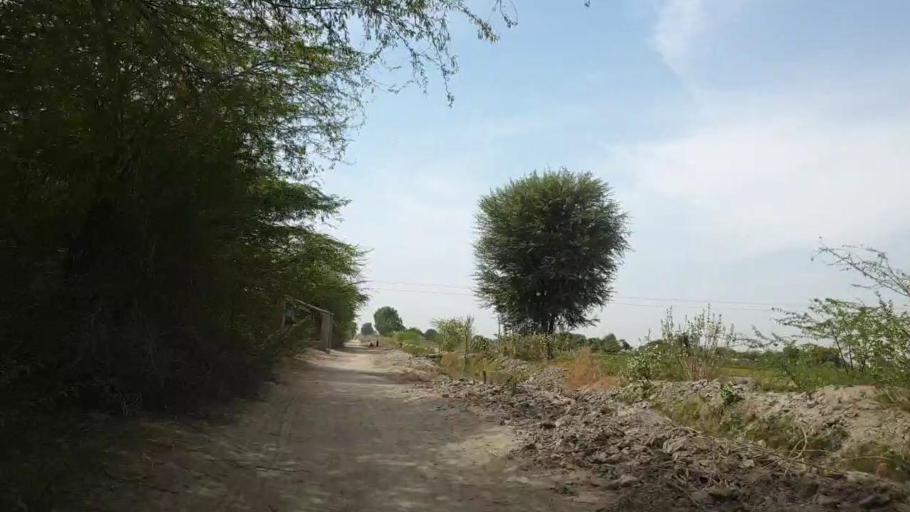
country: PK
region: Sindh
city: Kunri
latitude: 25.1945
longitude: 69.5773
